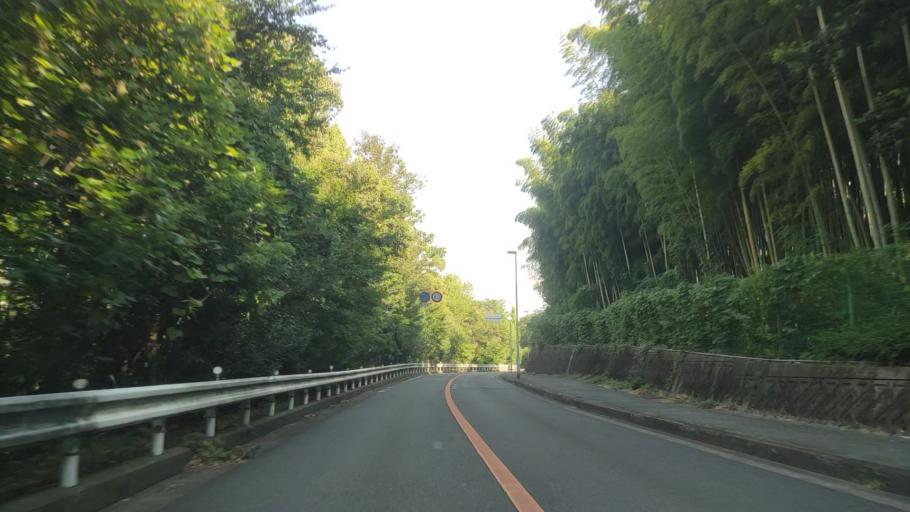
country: JP
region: Osaka
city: Mino
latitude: 34.8128
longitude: 135.5176
